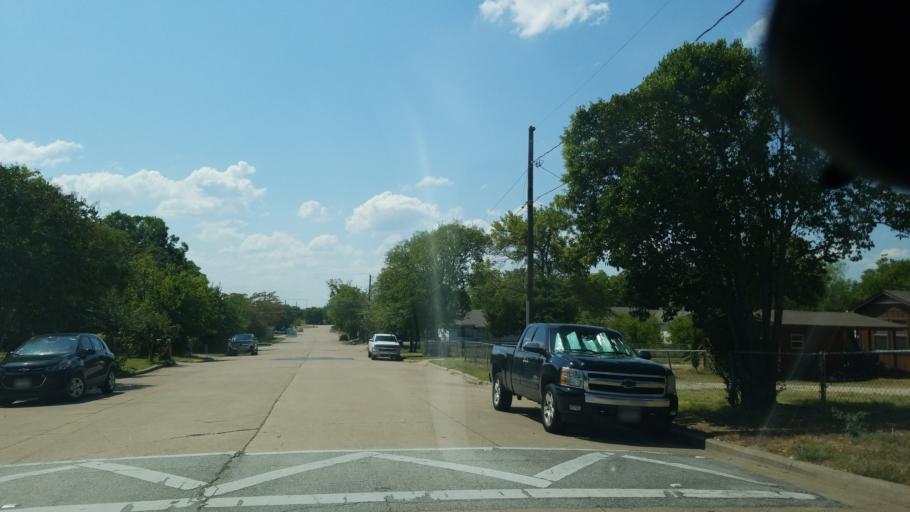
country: US
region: Texas
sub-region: Dallas County
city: Grand Prairie
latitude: 32.7088
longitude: -96.9815
